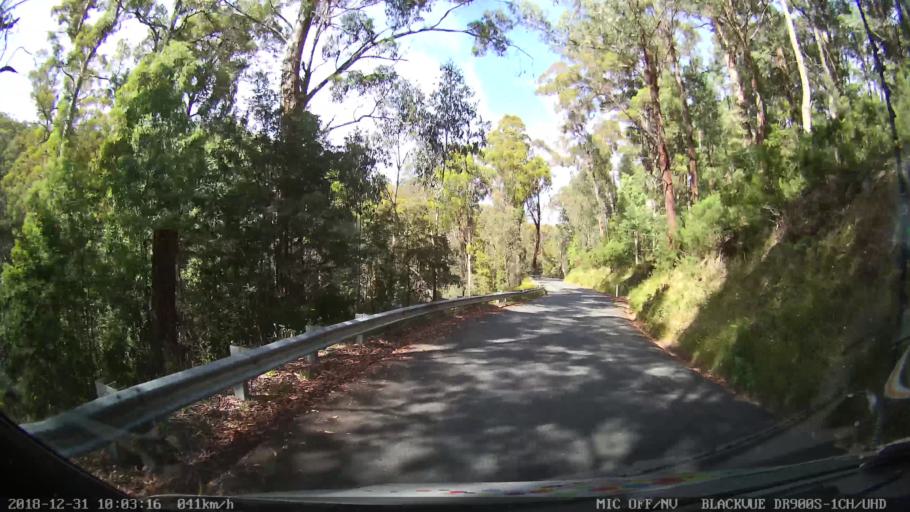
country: AU
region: New South Wales
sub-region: Snowy River
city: Jindabyne
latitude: -36.5321
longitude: 148.1926
